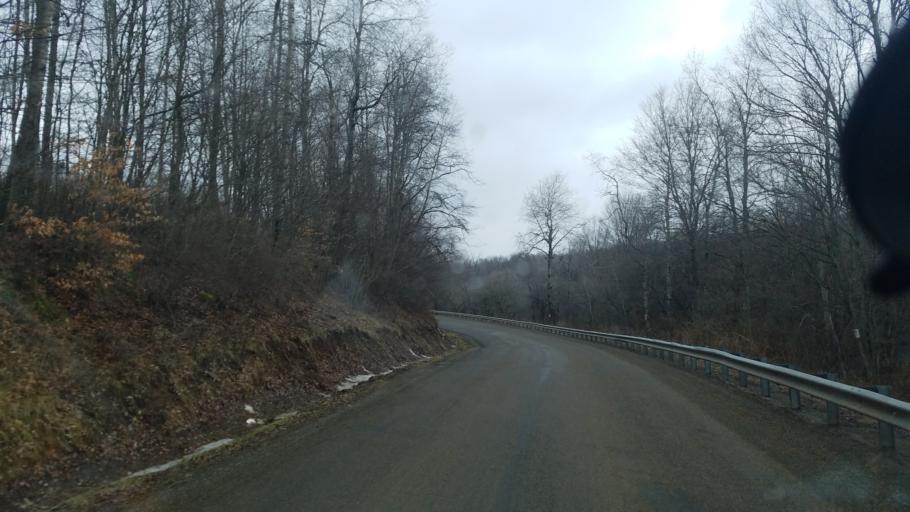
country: US
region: New York
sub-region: Allegany County
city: Andover
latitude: 41.9377
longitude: -77.8049
